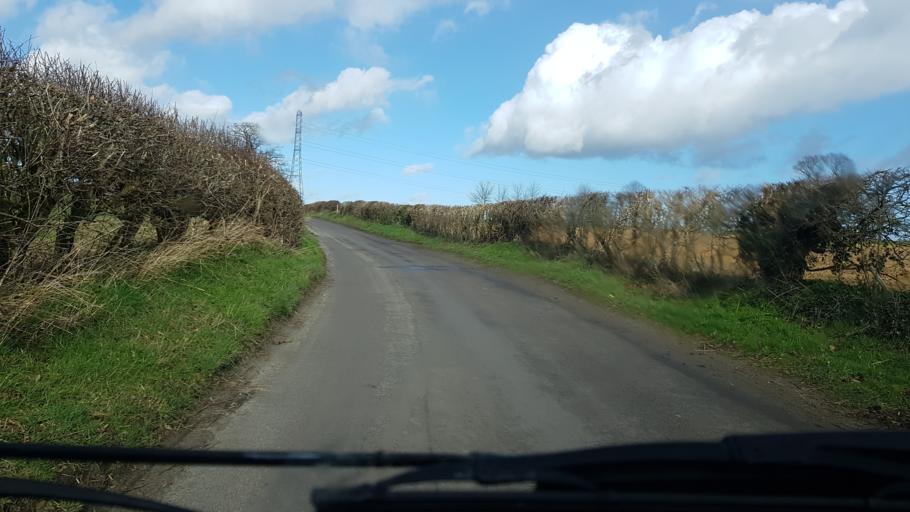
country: GB
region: England
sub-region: Wiltshire
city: Wilsford
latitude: 51.3265
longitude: -1.8661
